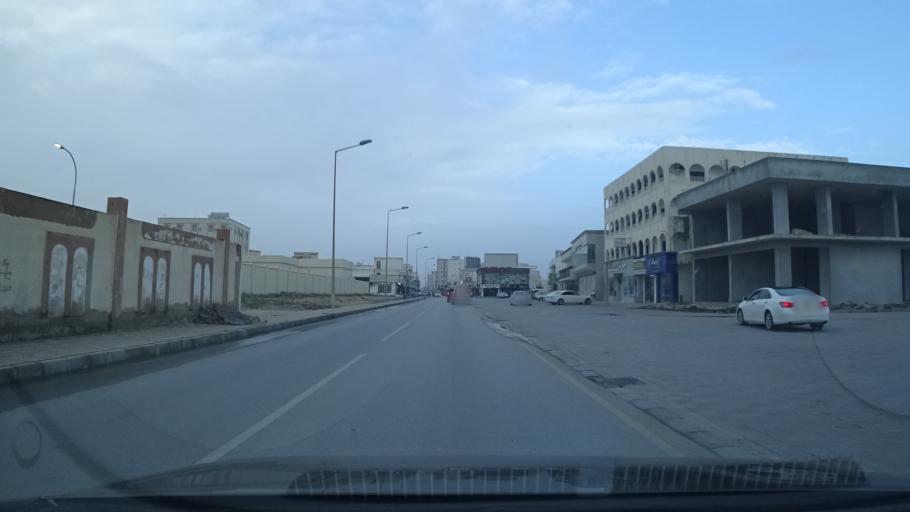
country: OM
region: Zufar
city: Salalah
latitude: 17.0089
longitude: 54.0770
